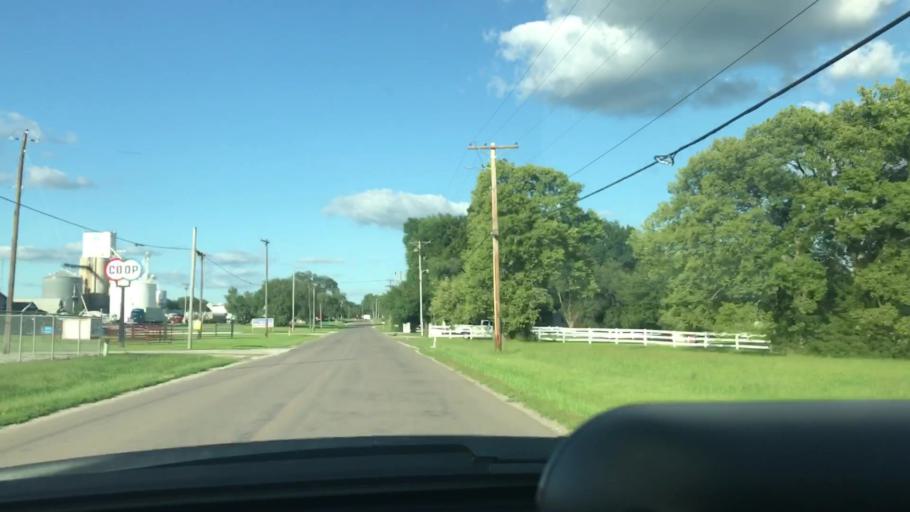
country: US
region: Missouri
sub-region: Pettis County
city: Sedalia
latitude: 38.6897
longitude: -93.2433
